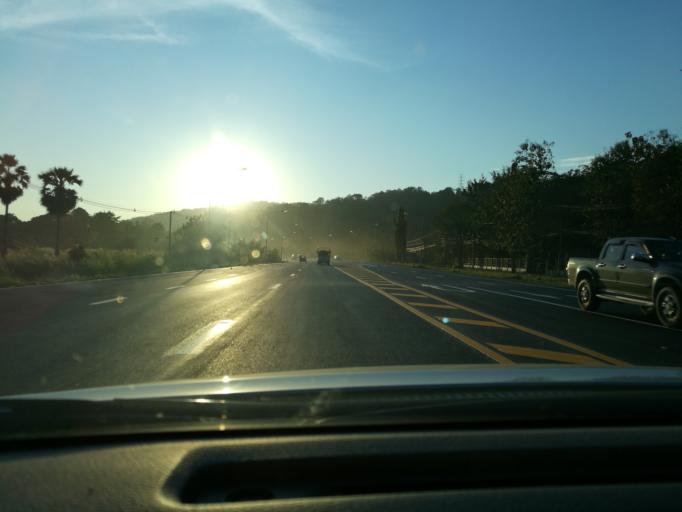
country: TH
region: Phitsanulok
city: Wang Thong
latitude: 16.8649
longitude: 100.4862
